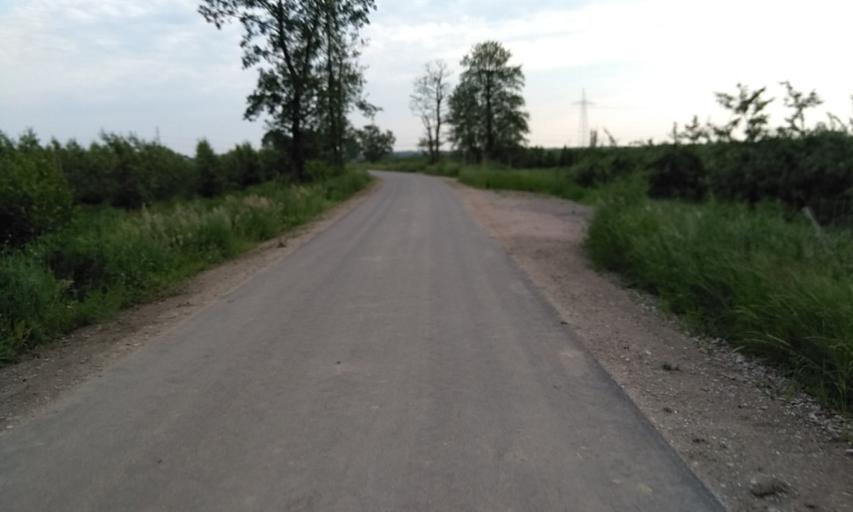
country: DE
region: Lower Saxony
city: Mittelnkirchen
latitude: 53.5148
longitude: 9.6364
